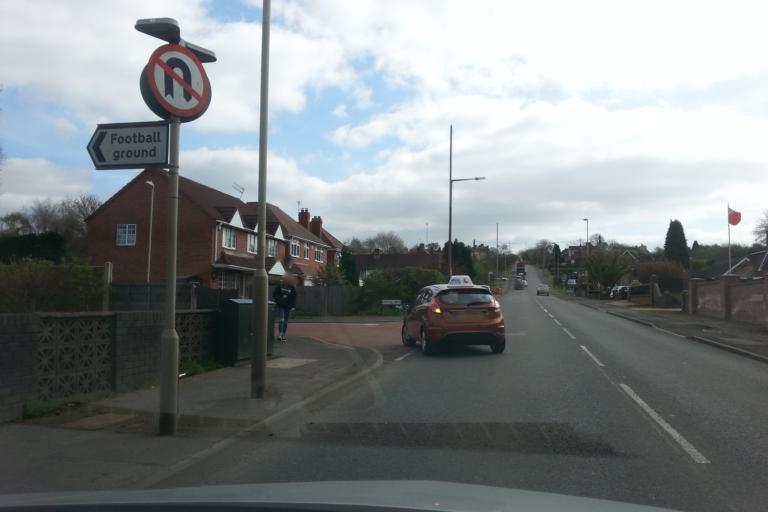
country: GB
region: England
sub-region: Dudley
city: Brierley Hill
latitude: 52.5140
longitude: -2.1297
